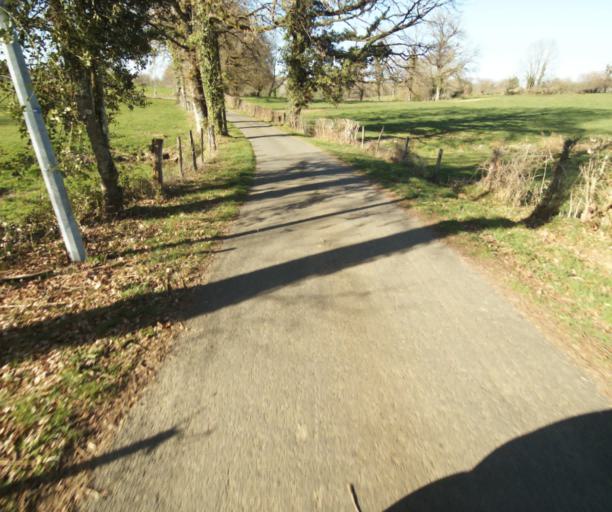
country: FR
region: Limousin
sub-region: Departement de la Correze
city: Seilhac
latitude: 45.3899
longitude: 1.6730
